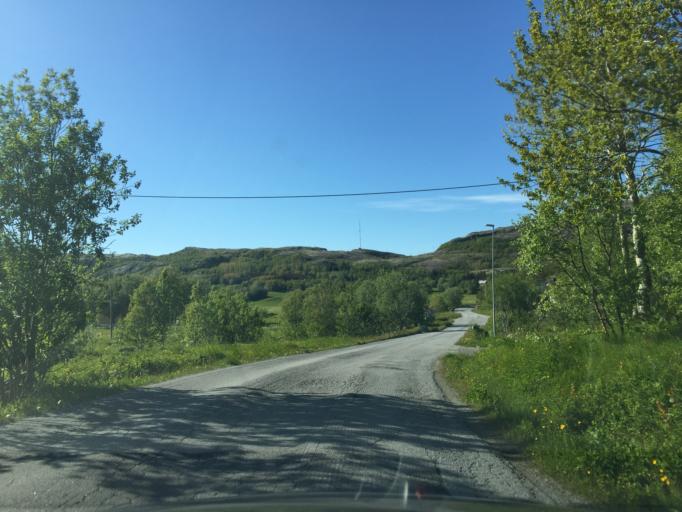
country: NO
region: Nordland
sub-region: Bodo
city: Loding
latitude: 67.4003
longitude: 14.6446
